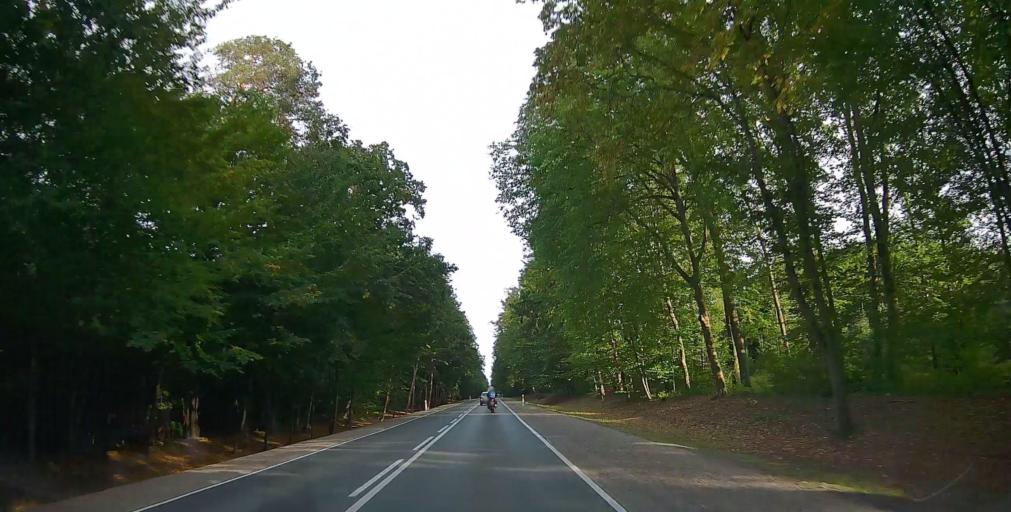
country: PL
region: Masovian Voivodeship
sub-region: Powiat piaseczynski
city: Zabieniec
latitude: 52.0465
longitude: 21.0742
